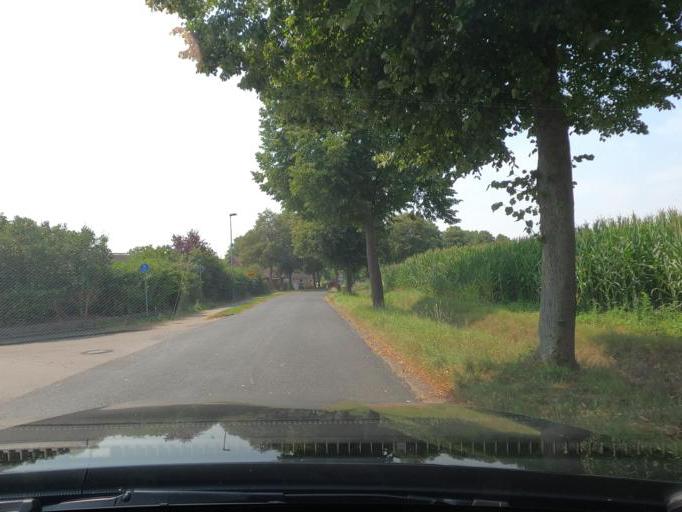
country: DE
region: Lower Saxony
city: Elze
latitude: 52.1747
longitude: 9.7231
